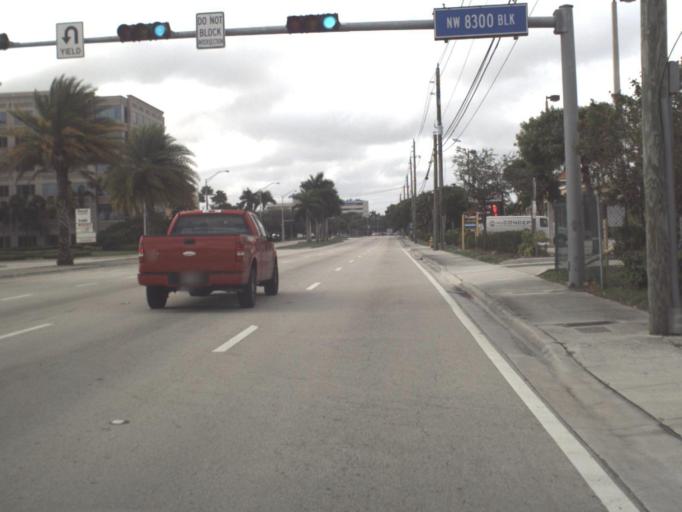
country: US
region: Florida
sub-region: Miami-Dade County
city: Doral
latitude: 25.8100
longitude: -80.3313
